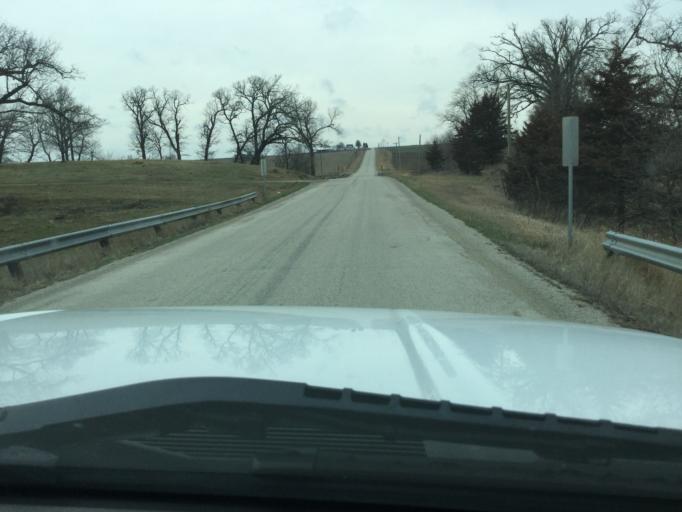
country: US
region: Kansas
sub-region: Nemaha County
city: Sabetha
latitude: 39.8536
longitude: -95.7142
